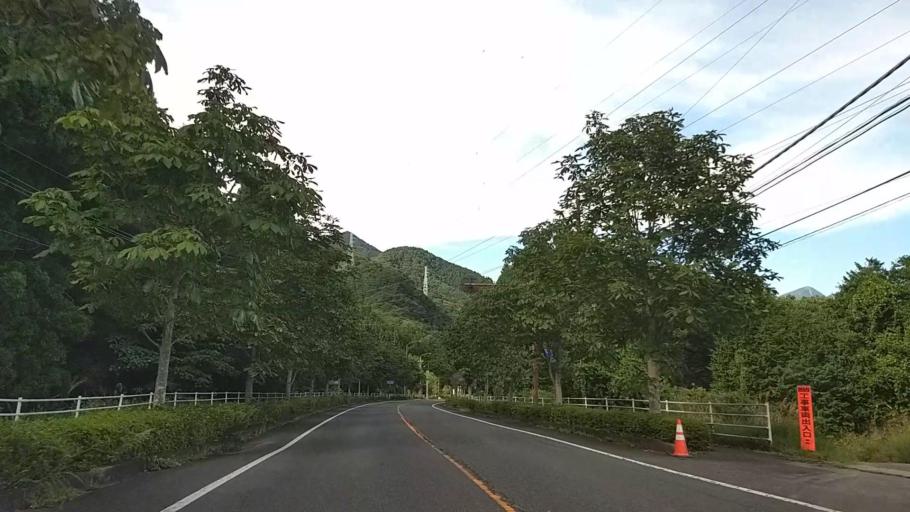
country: JP
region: Tochigi
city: Imaichi
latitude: 36.8142
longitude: 139.7069
